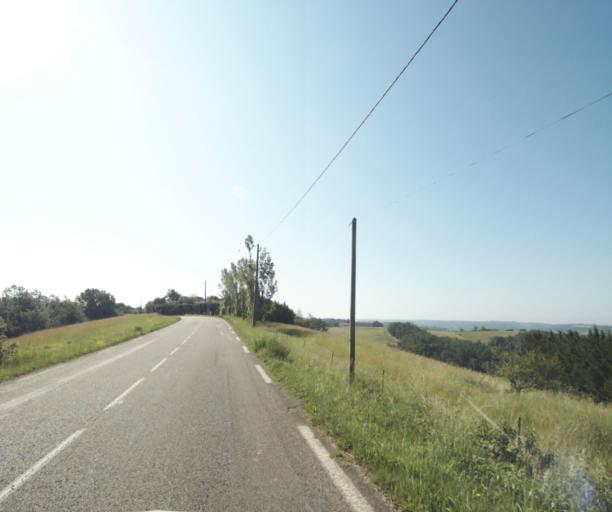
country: FR
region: Midi-Pyrenees
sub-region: Departement du Tarn-et-Garonne
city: Saint-Nauphary
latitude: 43.9856
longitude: 1.4311
